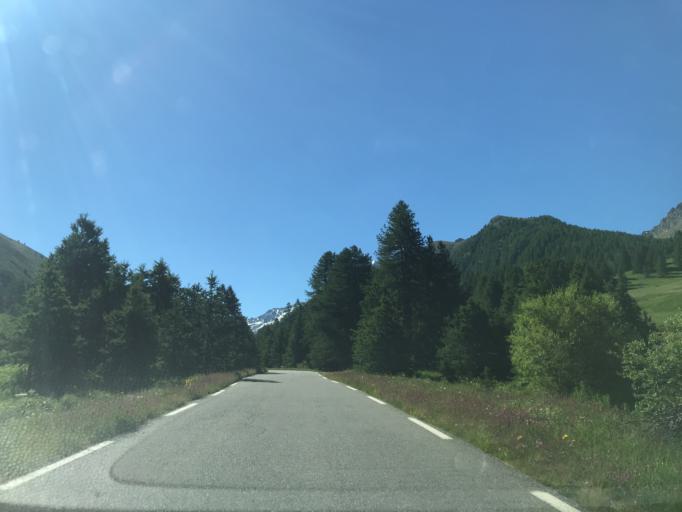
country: IT
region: Piedmont
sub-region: Provincia di Cuneo
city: Pontechianale
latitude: 44.7175
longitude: 6.9105
